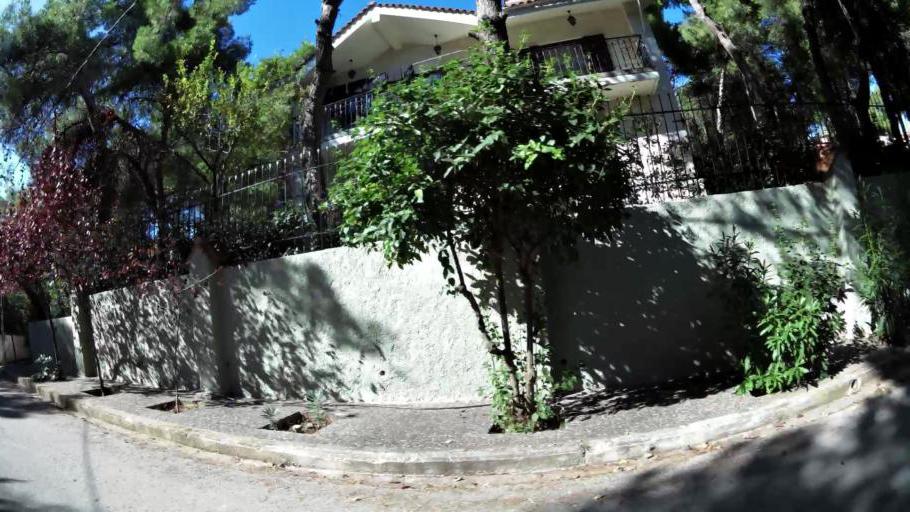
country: GR
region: Attica
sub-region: Nomarchia Anatolikis Attikis
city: Dionysos
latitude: 38.1024
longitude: 23.8868
